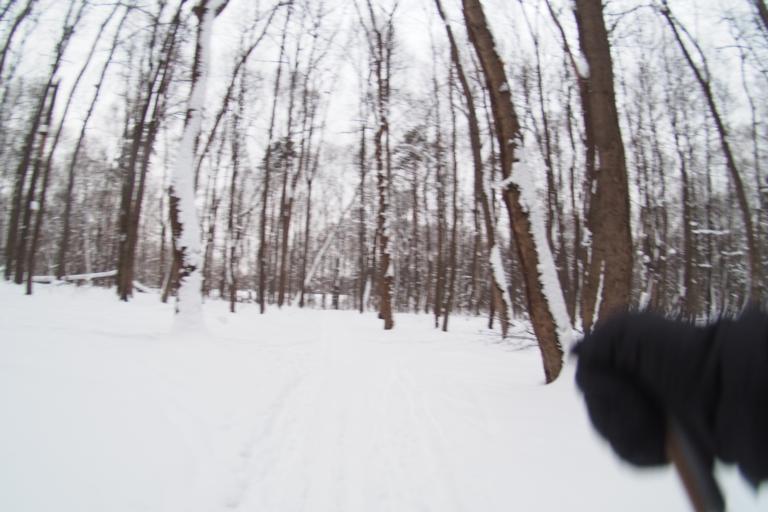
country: RU
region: Moskovskaya
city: Izmaylovo
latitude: 55.7777
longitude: 37.7838
